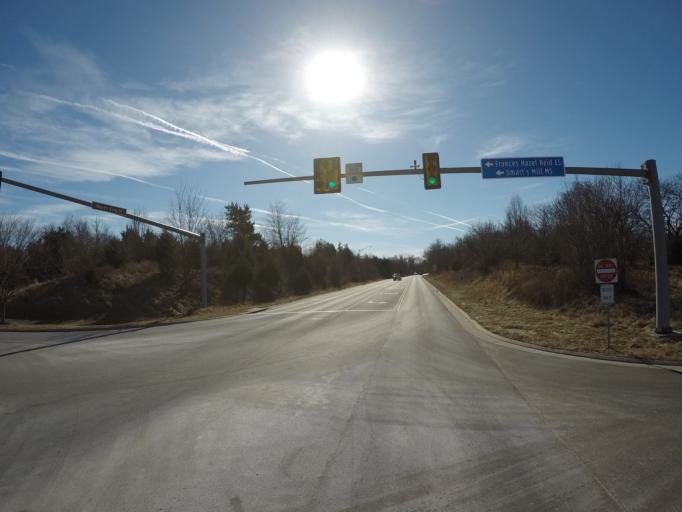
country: US
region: Virginia
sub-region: Loudoun County
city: Leesburg
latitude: 39.1331
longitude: -77.5513
